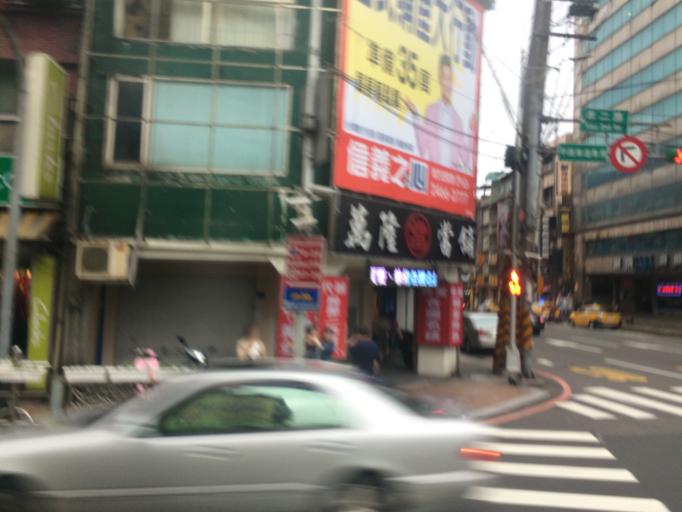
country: TW
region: Taiwan
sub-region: Keelung
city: Keelung
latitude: 25.1284
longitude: 121.7394
